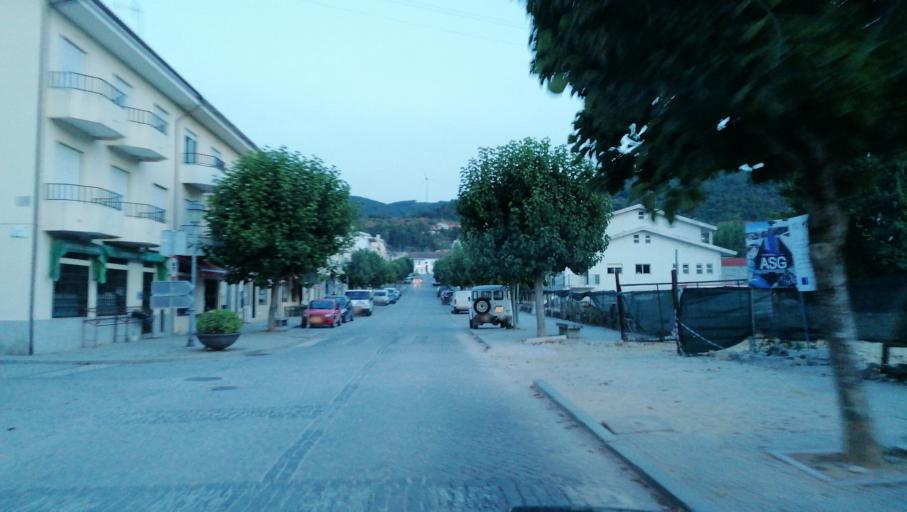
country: PT
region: Vila Real
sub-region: Vila Pouca de Aguiar
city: Vila Pouca de Aguiar
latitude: 41.5442
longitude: -7.6054
